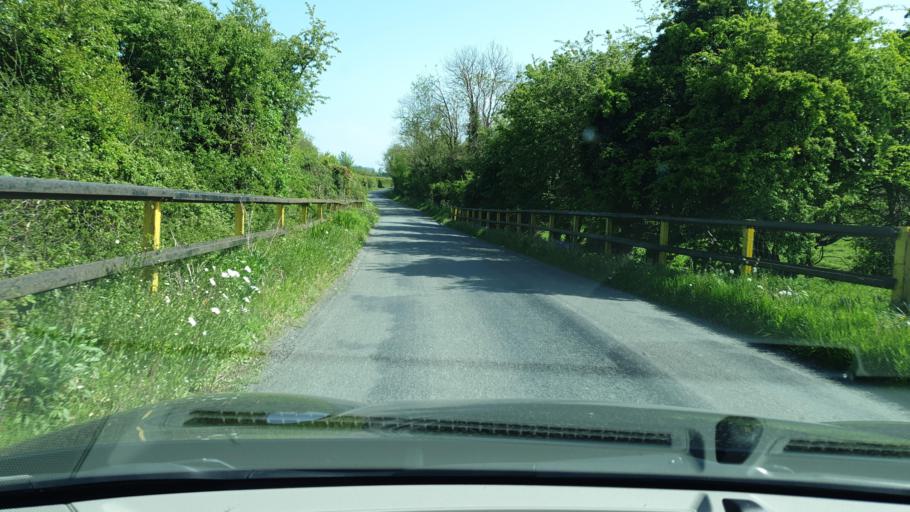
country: IE
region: Leinster
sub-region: An Mhi
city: Dunshaughlin
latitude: 53.4754
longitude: -6.5403
